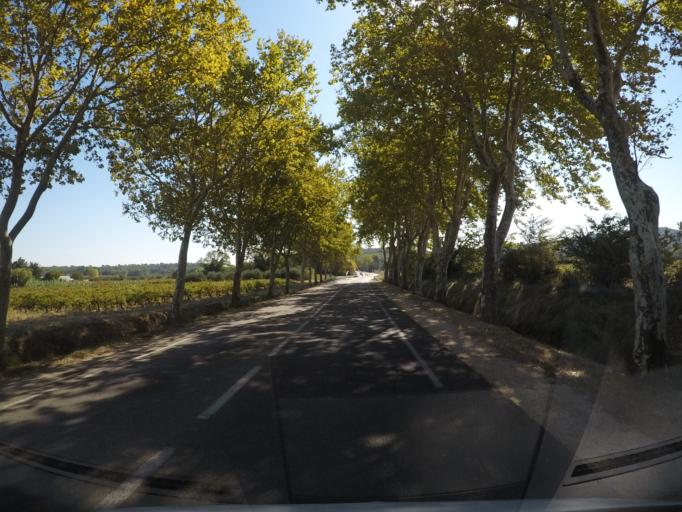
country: FR
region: Languedoc-Roussillon
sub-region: Departement du Gard
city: Castillon-du-Gard
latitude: 43.9615
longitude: 4.5164
